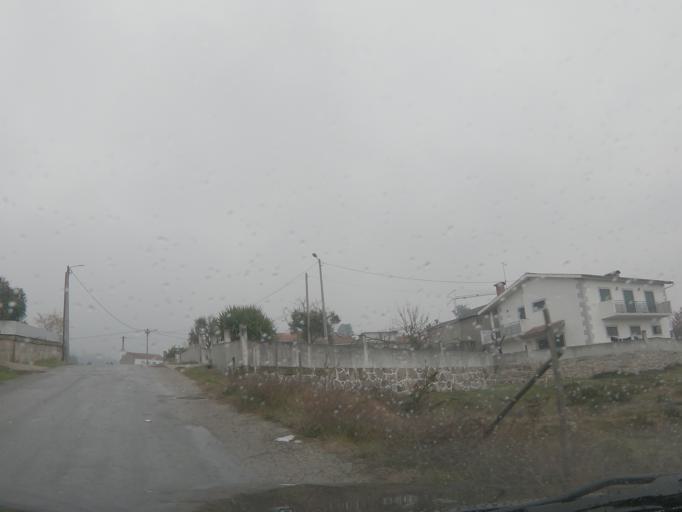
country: PT
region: Vila Real
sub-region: Vila Real
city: Vila Real
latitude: 41.3029
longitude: -7.7829
